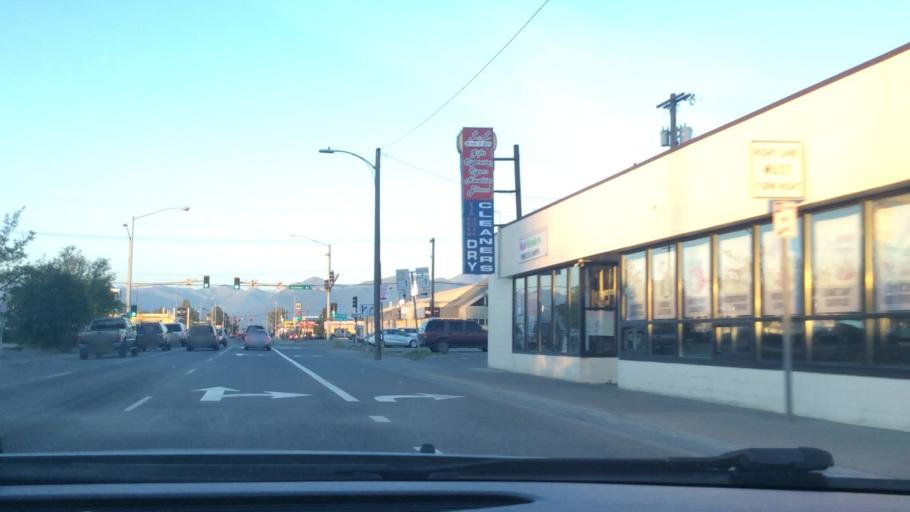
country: US
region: Alaska
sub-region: Anchorage Municipality
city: Anchorage
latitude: 61.2166
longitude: -149.8727
